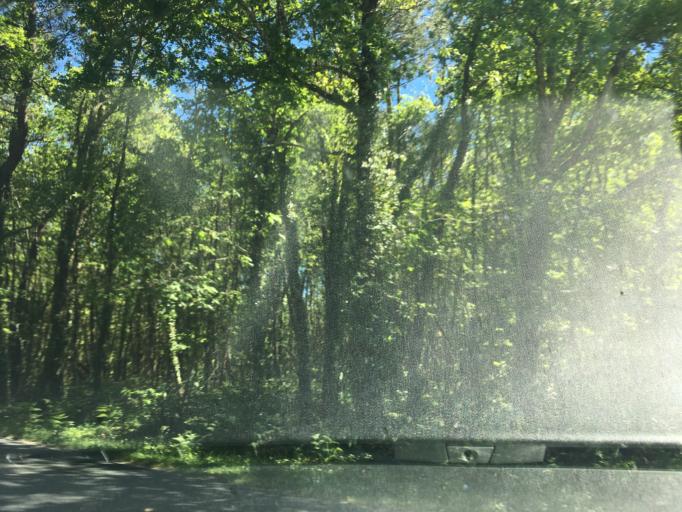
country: FR
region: Aquitaine
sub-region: Departement de la Gironde
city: Lesparre-Medoc
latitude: 45.2863
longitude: -0.8986
